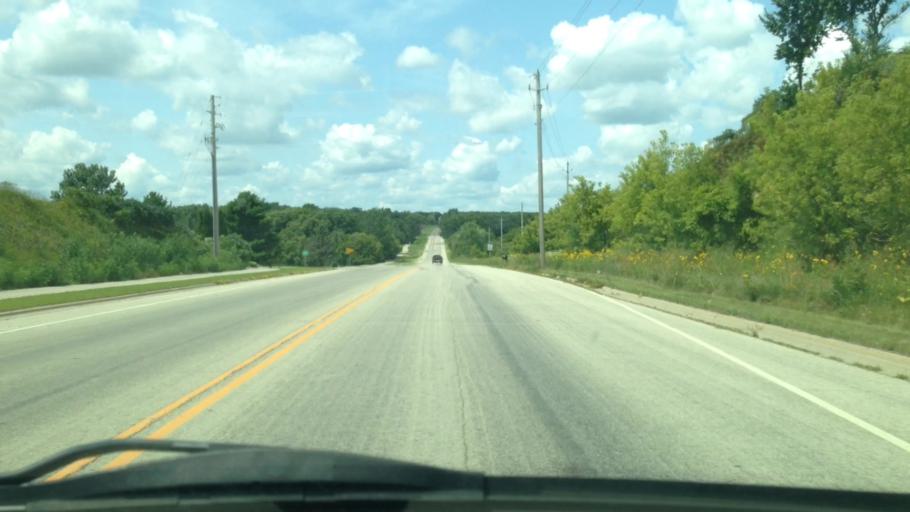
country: US
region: Minnesota
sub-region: Olmsted County
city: Rochester
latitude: 43.9531
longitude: -92.4880
